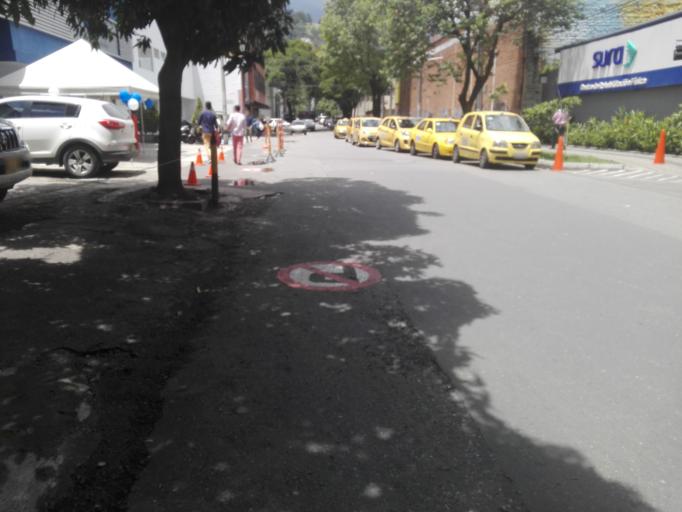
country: CO
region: Antioquia
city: Medellin
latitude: 6.2288
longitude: -75.5736
